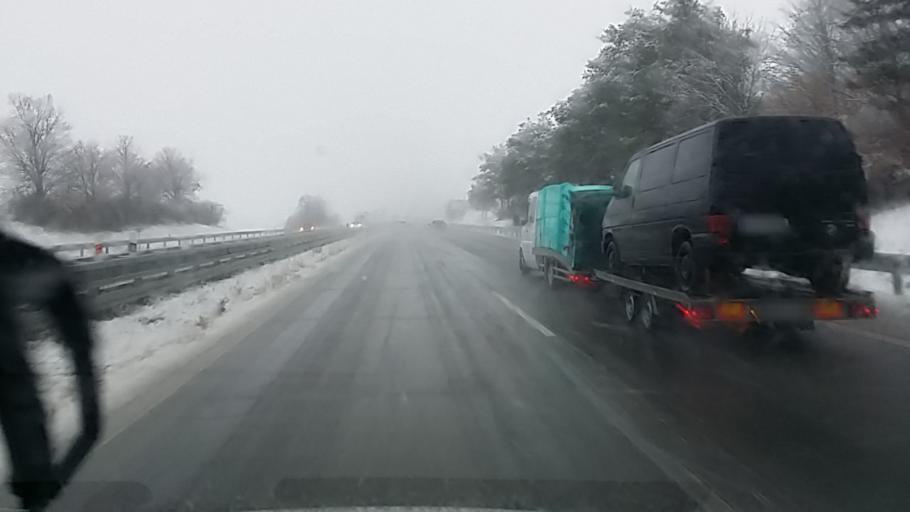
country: CZ
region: South Moravian
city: Krepice
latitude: 48.9700
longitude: 16.7078
